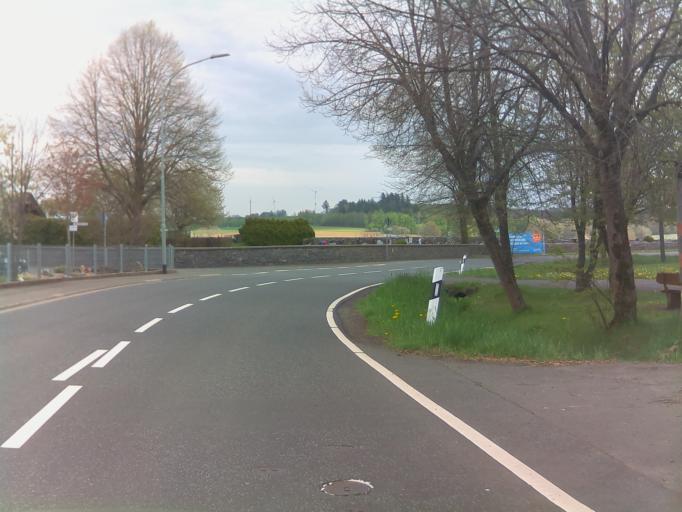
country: DE
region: Hesse
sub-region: Regierungsbezirk Giessen
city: Grebenhain
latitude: 50.4704
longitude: 9.3196
